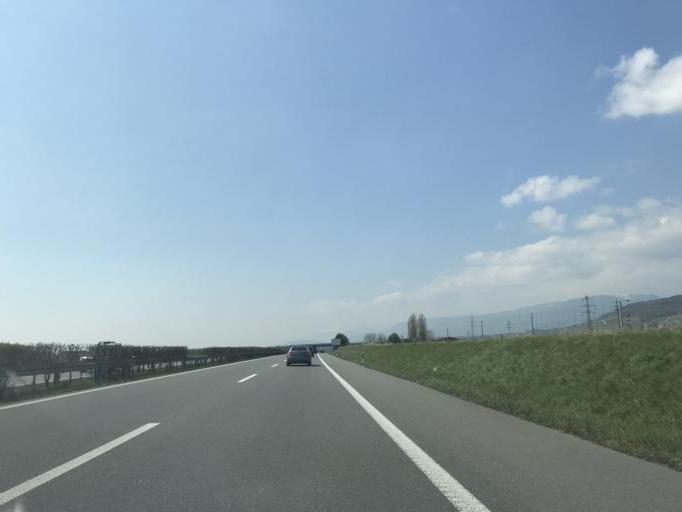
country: CH
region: Vaud
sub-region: Nyon District
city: Rolle
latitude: 46.4507
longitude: 6.3084
